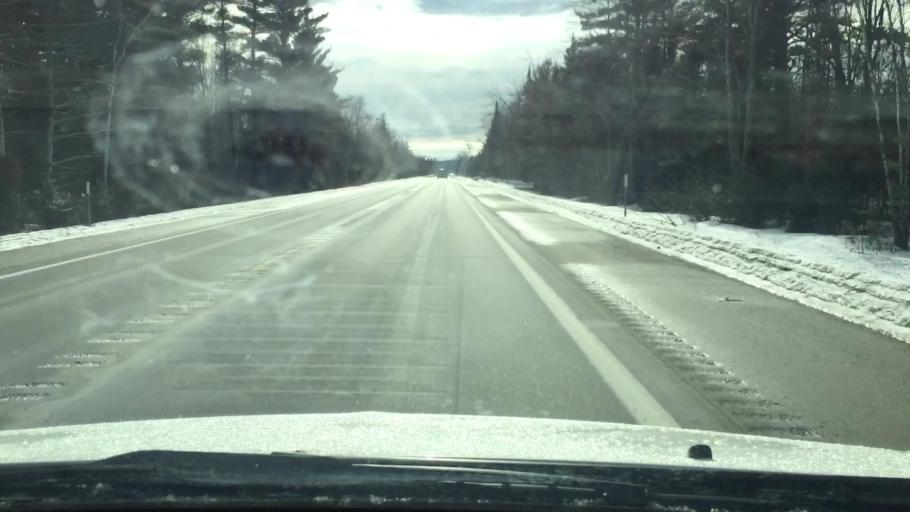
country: US
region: Michigan
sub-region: Kalkaska County
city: Kalkaska
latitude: 44.7119
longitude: -85.1940
